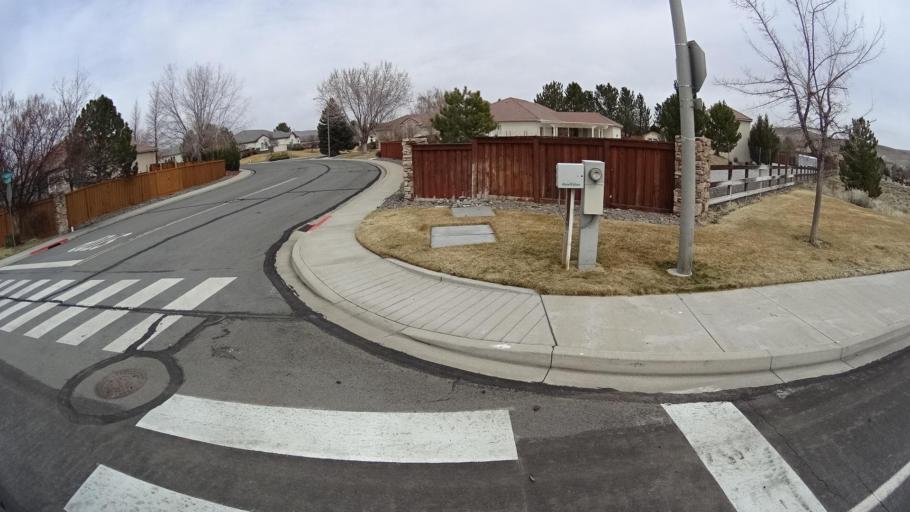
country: US
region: Nevada
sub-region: Washoe County
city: Spanish Springs
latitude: 39.6338
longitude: -119.6868
